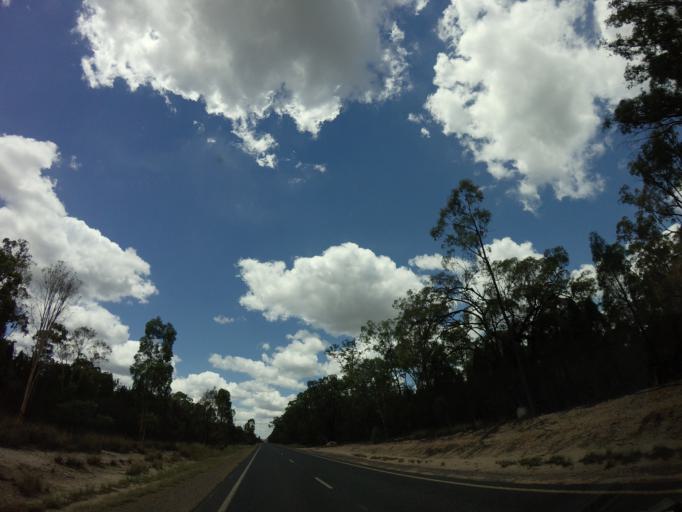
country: AU
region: New South Wales
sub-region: Moree Plains
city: Boggabilla
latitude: -27.9898
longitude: 150.9613
